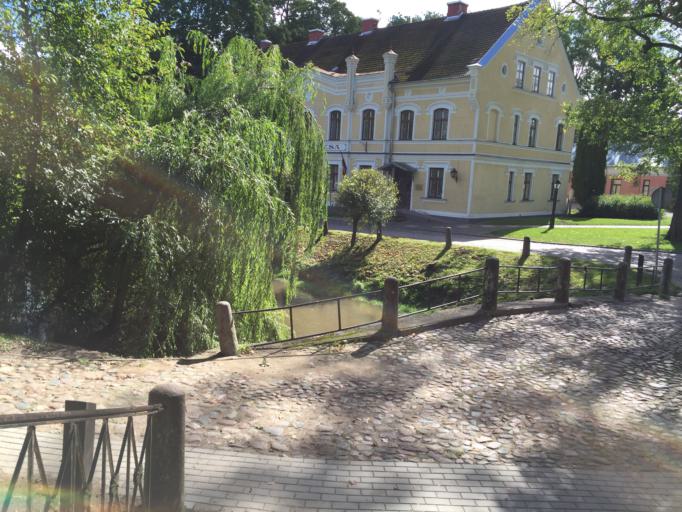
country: LV
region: Kuldigas Rajons
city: Kuldiga
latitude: 56.9699
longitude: 21.9737
